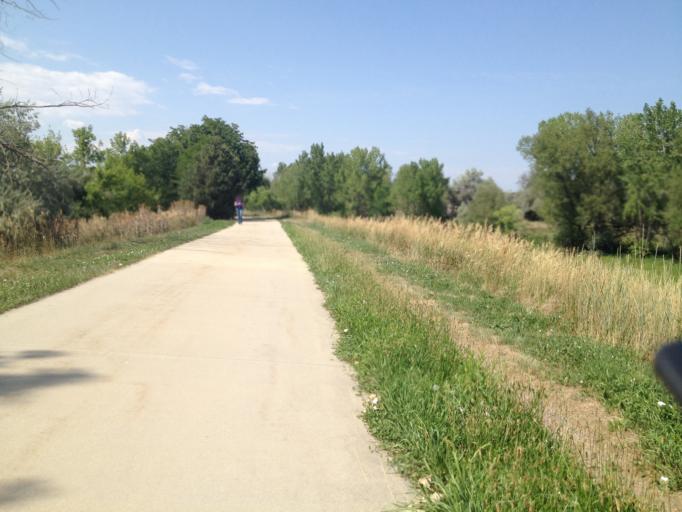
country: US
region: Colorado
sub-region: Boulder County
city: Boulder
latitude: 40.0245
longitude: -105.2169
